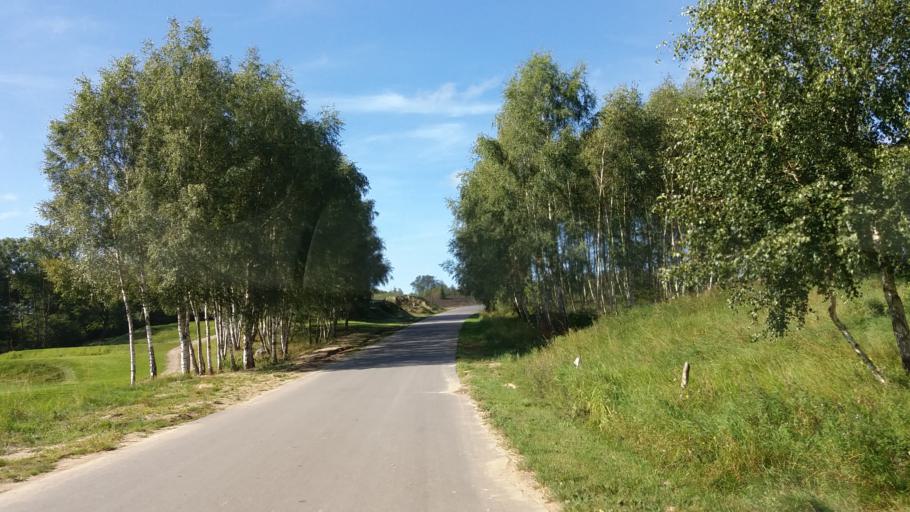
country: PL
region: West Pomeranian Voivodeship
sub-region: Powiat choszczenski
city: Krzecin
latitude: 53.1351
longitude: 15.4795
